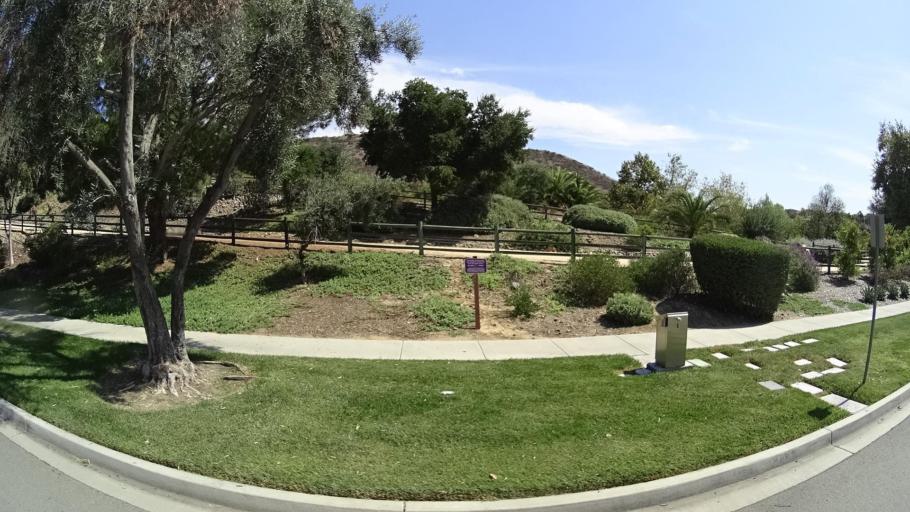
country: US
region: California
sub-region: San Diego County
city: La Presa
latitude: 32.6645
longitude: -116.9713
